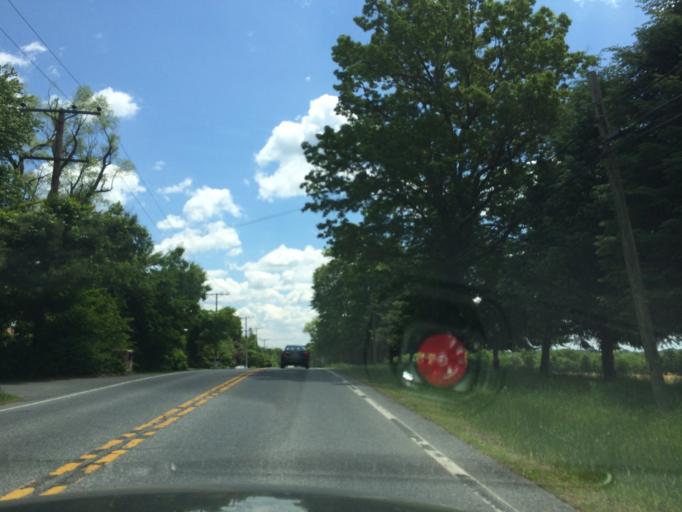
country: US
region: Maryland
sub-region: Howard County
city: Columbia
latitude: 39.2845
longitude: -76.8861
